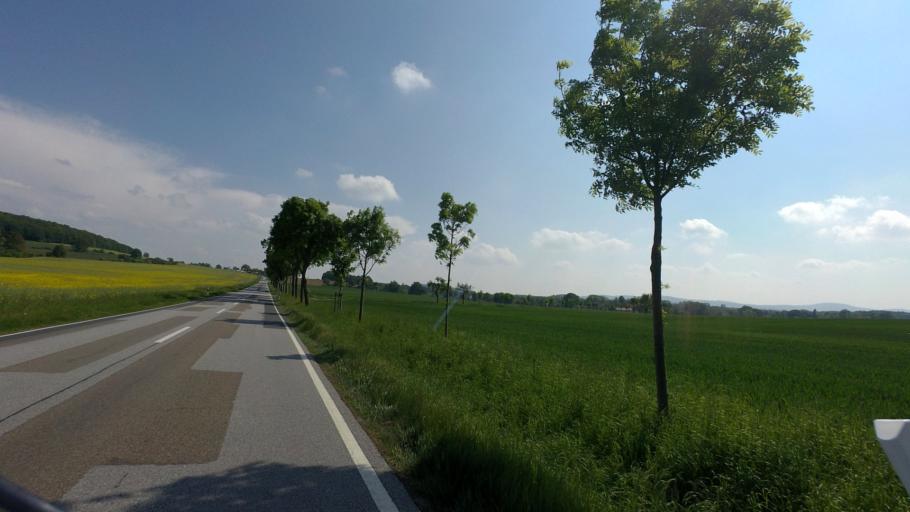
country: DE
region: Saxony
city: Weissenberg
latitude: 51.1847
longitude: 14.6432
